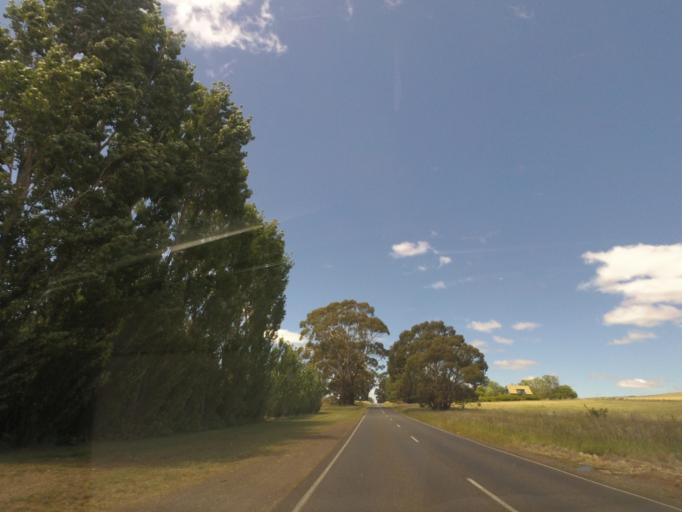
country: AU
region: Victoria
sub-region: Mount Alexander
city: Castlemaine
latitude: -37.3224
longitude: 144.1980
